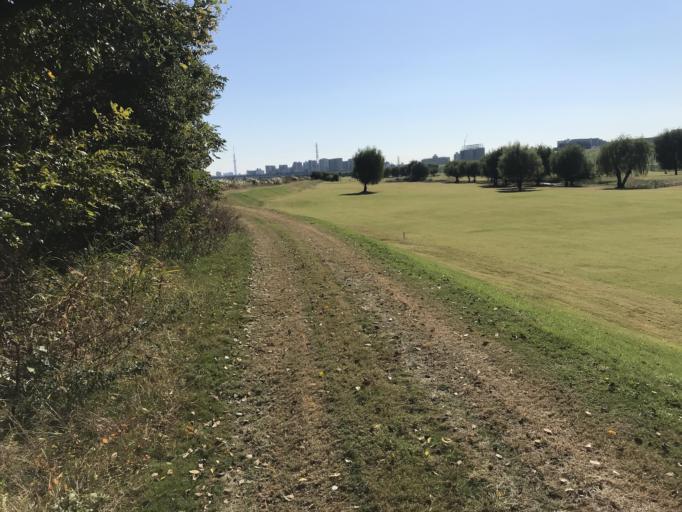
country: JP
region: Saitama
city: Kawaguchi
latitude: 35.7849
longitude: 139.7379
